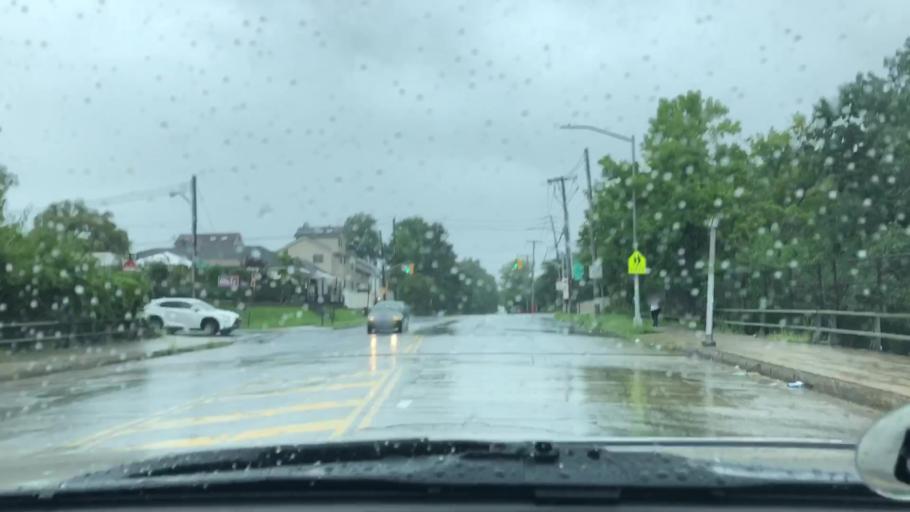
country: US
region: New Jersey
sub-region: Middlesex County
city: Carteret
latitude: 40.5351
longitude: -74.1934
